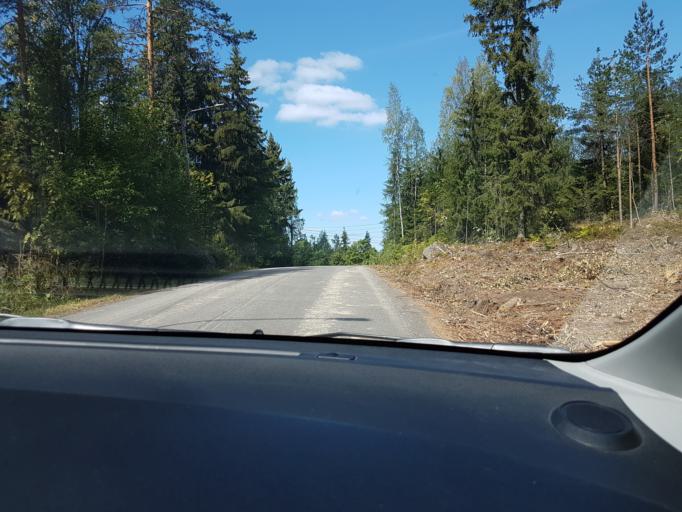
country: FI
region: Uusimaa
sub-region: Helsinki
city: Kilo
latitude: 60.3282
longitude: 24.7642
